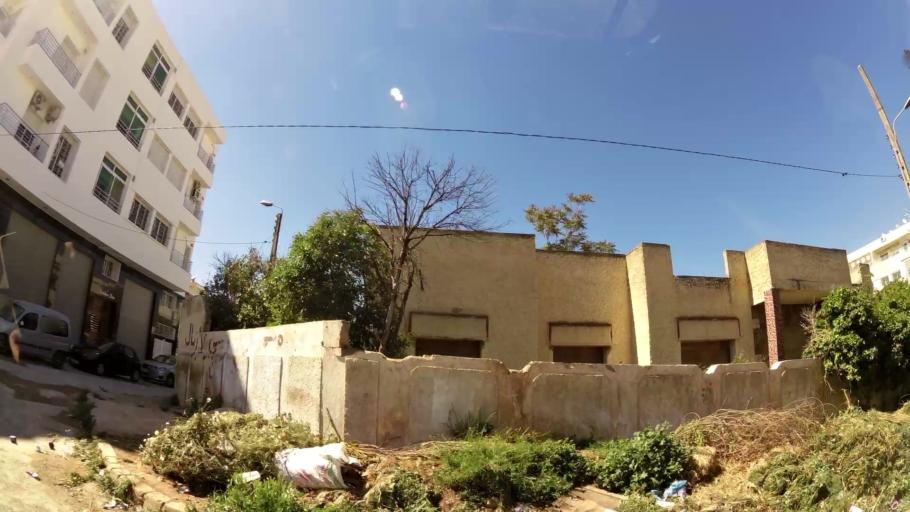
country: MA
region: Fes-Boulemane
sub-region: Fes
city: Fes
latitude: 34.0221
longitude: -4.9897
